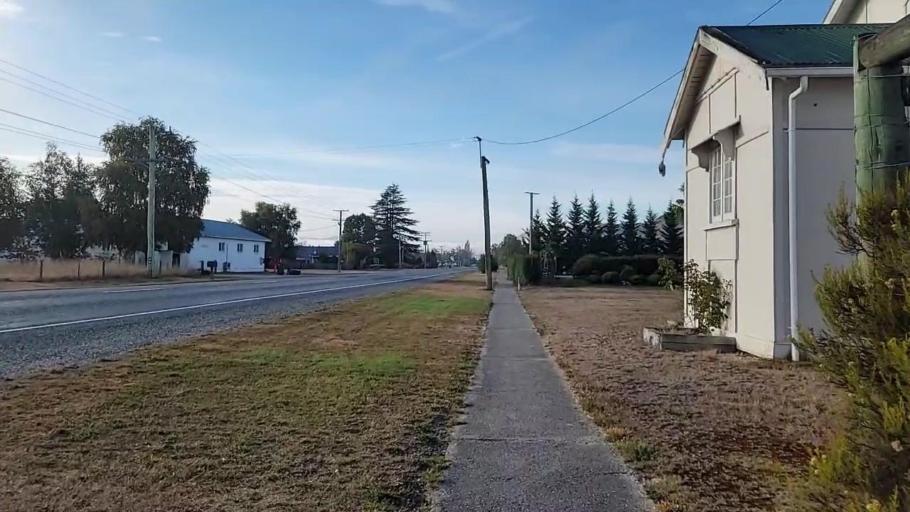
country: NZ
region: Southland
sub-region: Gore District
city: Gore
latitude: -45.6371
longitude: 169.3674
